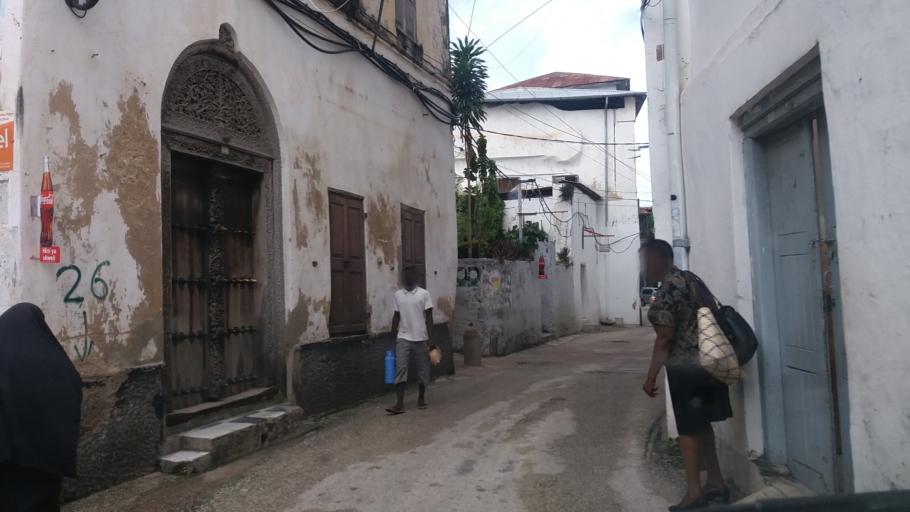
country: TZ
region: Zanzibar Urban/West
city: Zanzibar
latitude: -6.1633
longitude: 39.1877
